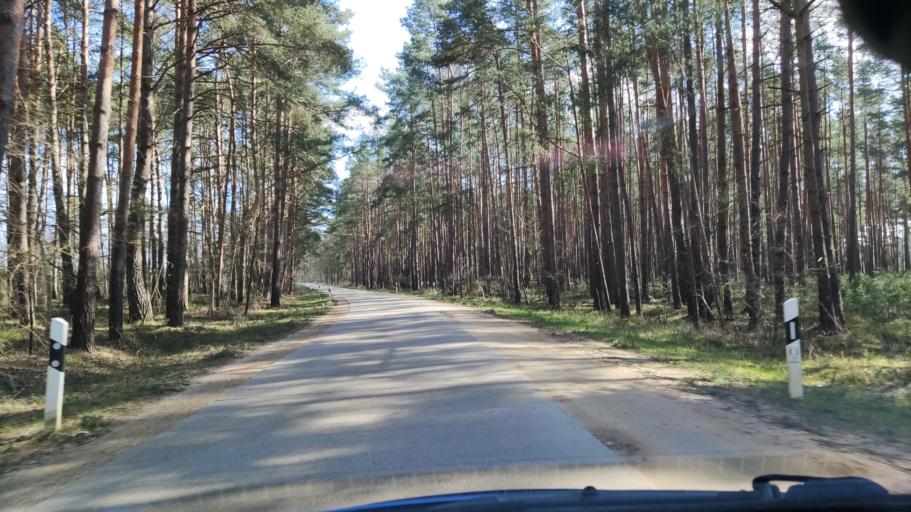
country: DE
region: Lower Saxony
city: Trebel
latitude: 52.9974
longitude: 11.2928
